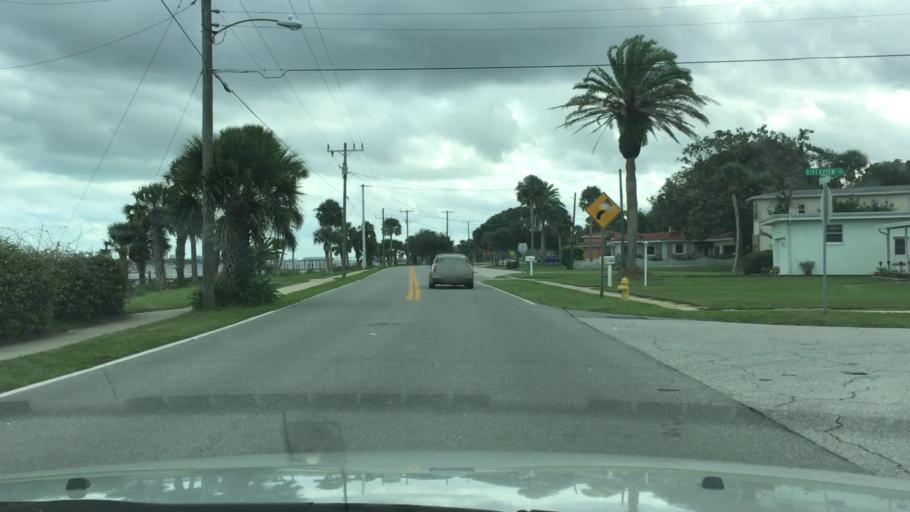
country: US
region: Florida
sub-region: Volusia County
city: Ormond Beach
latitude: 29.2716
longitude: -81.0481
